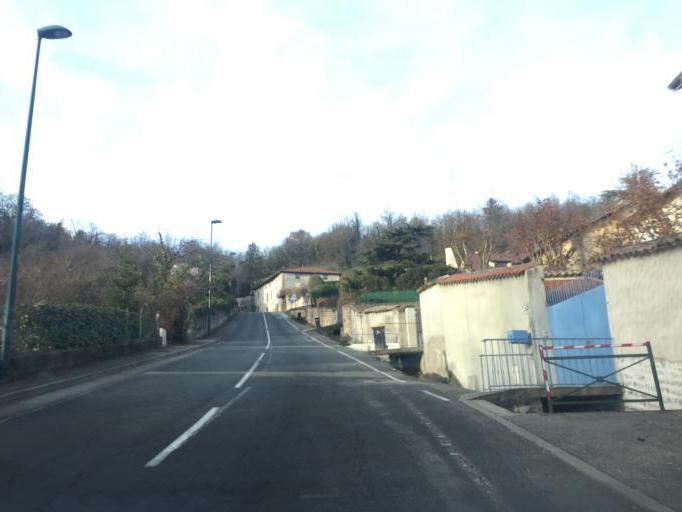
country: FR
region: Rhone-Alpes
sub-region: Departement de l'Ain
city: Miribel
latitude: 45.8283
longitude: 4.9534
